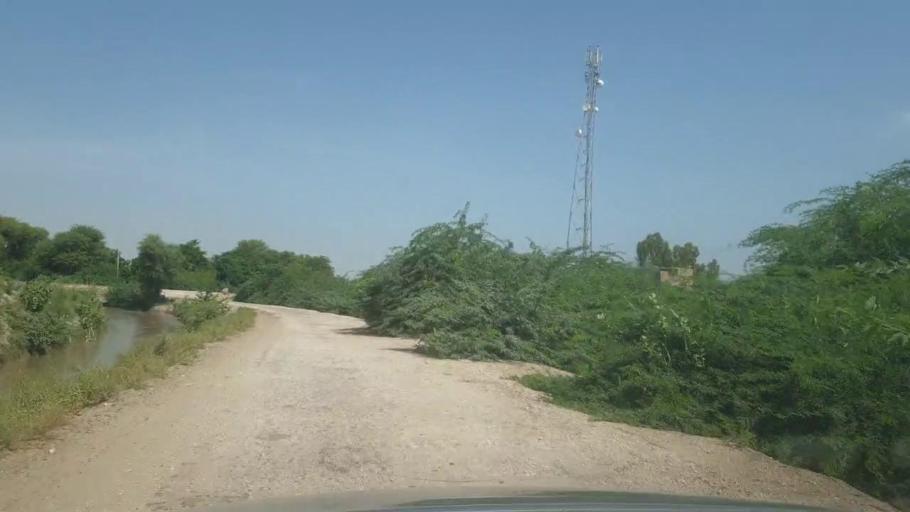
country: PK
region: Sindh
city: Khairpur
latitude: 27.4038
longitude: 69.0353
